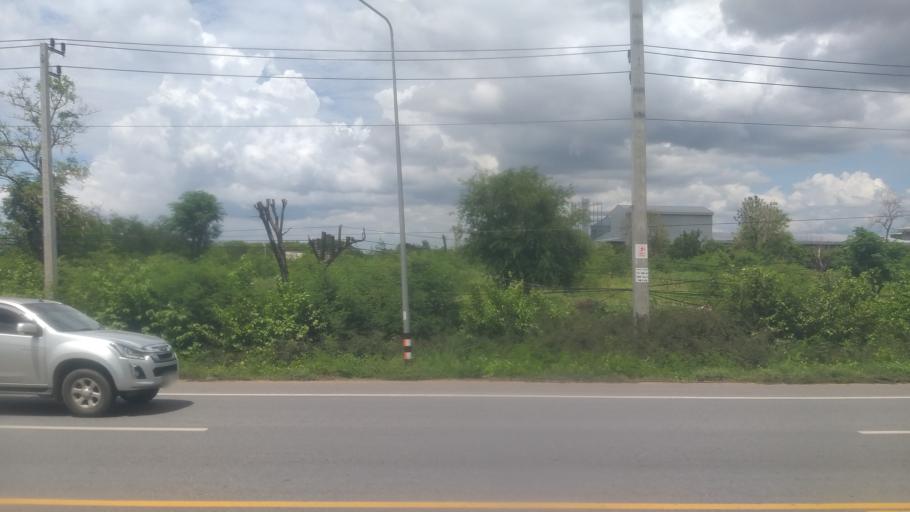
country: TH
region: Nakhon Ratchasima
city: Non Thai
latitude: 15.1097
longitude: 102.1011
